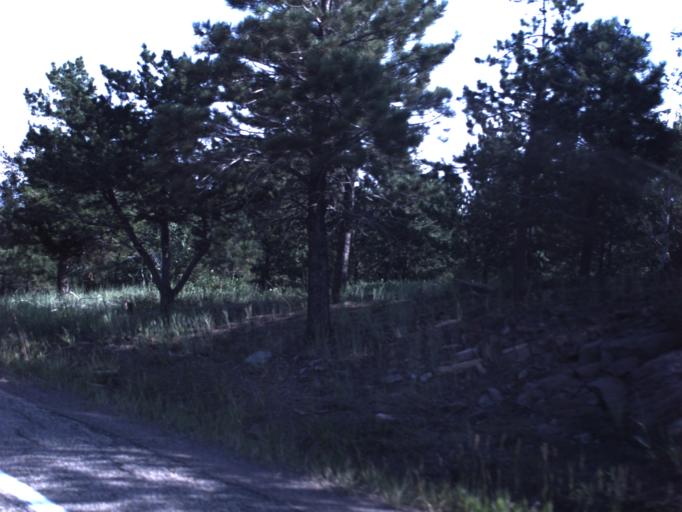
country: US
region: Utah
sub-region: Daggett County
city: Manila
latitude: 40.8549
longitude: -109.4625
